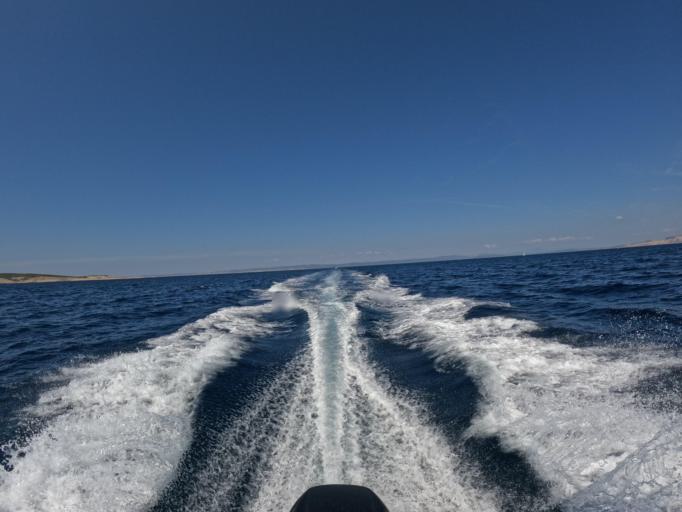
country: HR
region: Primorsko-Goranska
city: Lopar
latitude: 44.8542
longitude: 14.7100
